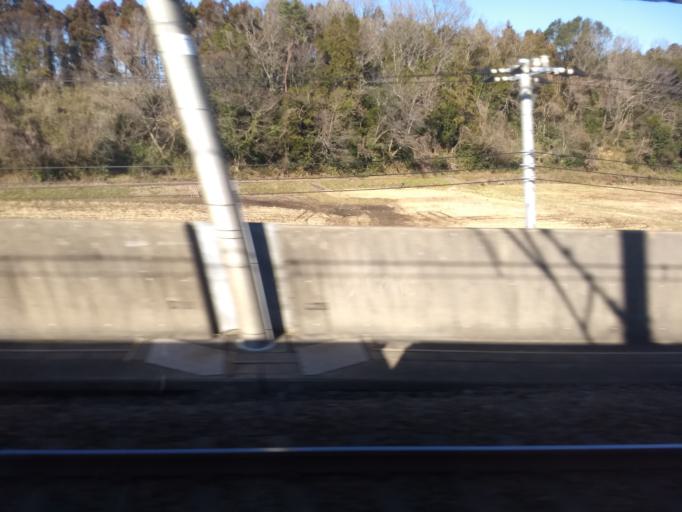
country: JP
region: Chiba
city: Narita
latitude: 35.7939
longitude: 140.3514
